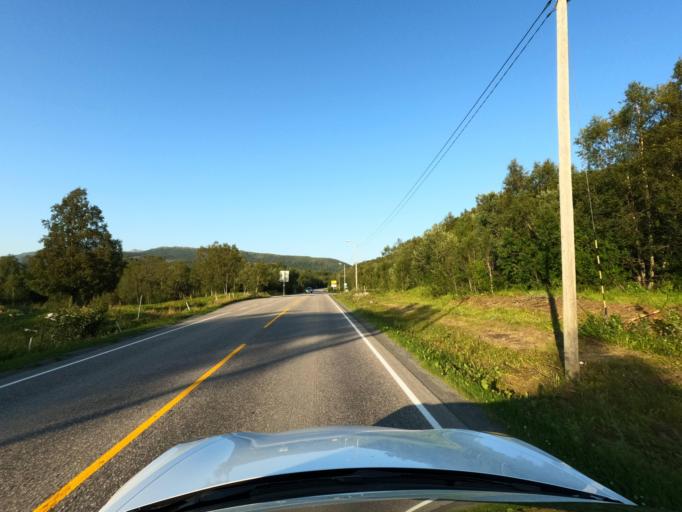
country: NO
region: Troms
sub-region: Skanland
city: Evenskjer
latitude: 68.4918
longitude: 16.7170
